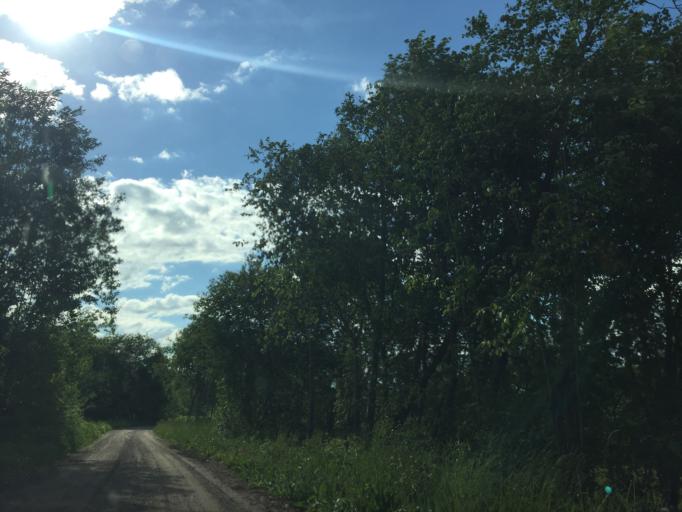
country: LV
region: Talsu Rajons
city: Sabile
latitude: 57.0121
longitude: 22.6345
